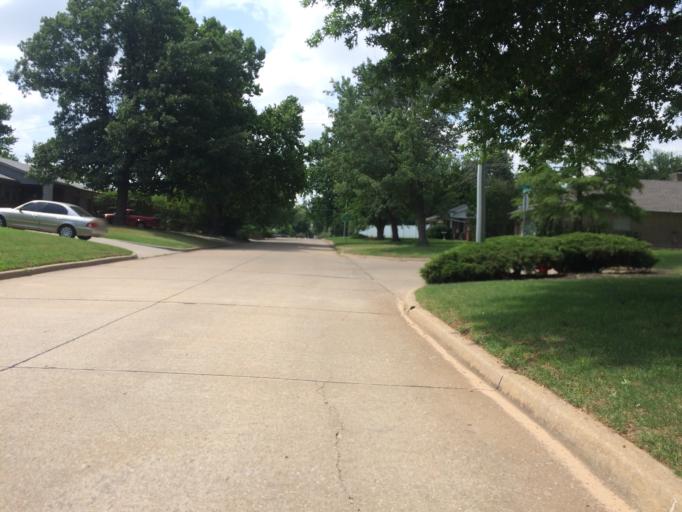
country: US
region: Oklahoma
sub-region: Cleveland County
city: Norman
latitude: 35.2104
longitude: -97.4815
